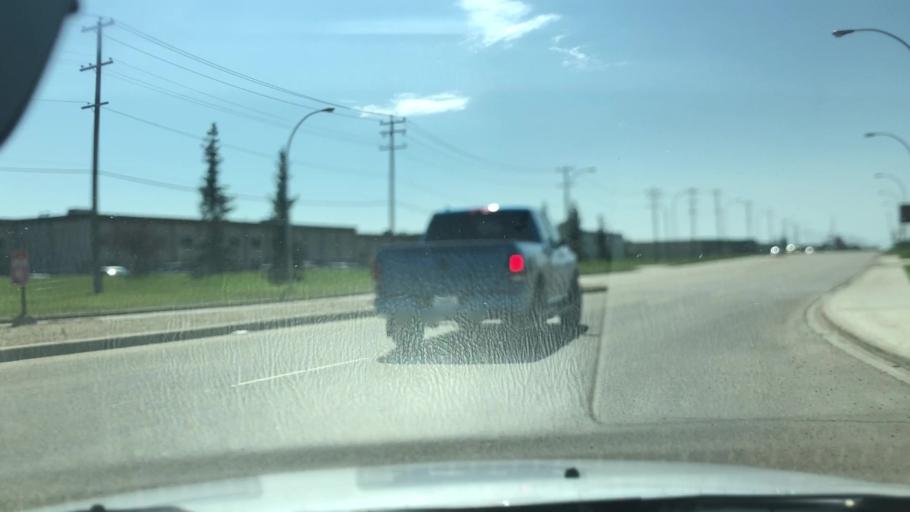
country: CA
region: Alberta
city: St. Albert
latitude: 53.5854
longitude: -113.5782
